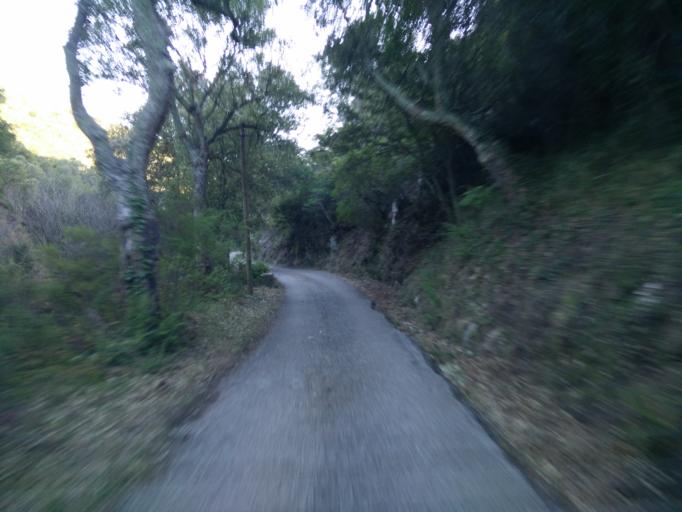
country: FR
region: Provence-Alpes-Cote d'Azur
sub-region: Departement du Var
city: Collobrieres
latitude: 43.2579
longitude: 6.3055
